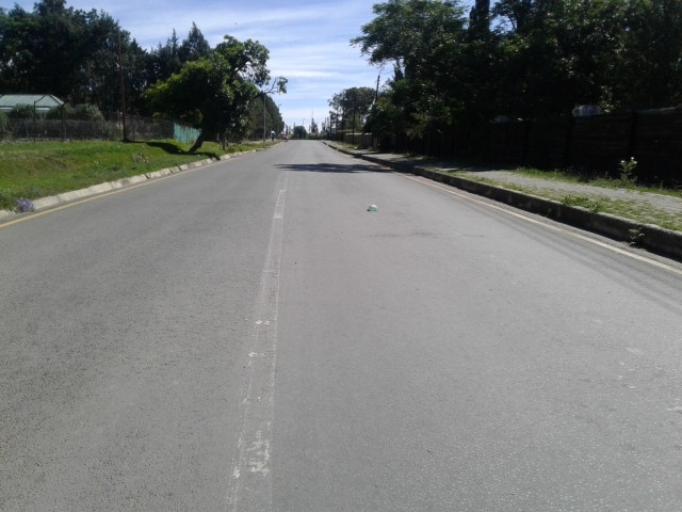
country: LS
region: Maseru
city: Maseru
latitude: -29.3076
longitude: 27.4813
